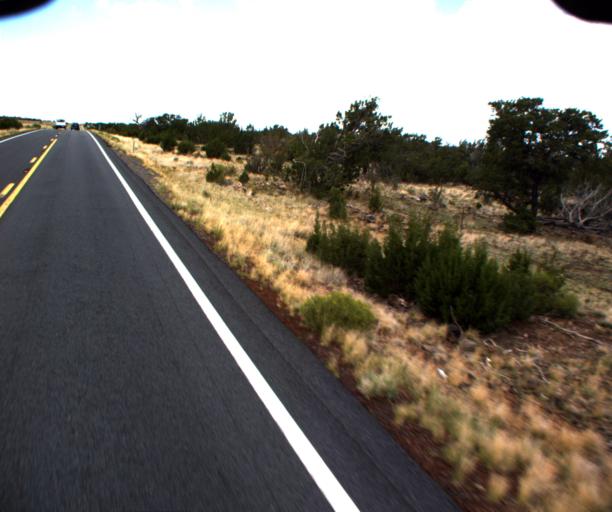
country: US
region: Arizona
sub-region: Coconino County
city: Parks
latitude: 35.5706
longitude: -111.9235
